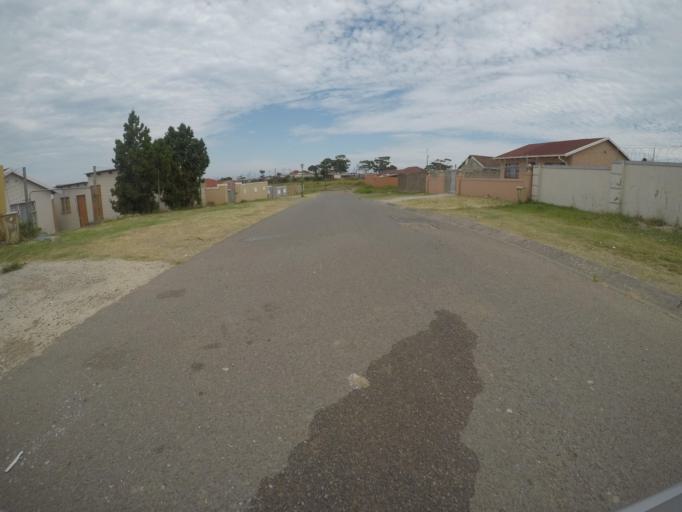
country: ZA
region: Eastern Cape
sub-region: Buffalo City Metropolitan Municipality
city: East London
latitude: -33.0022
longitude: 27.8751
